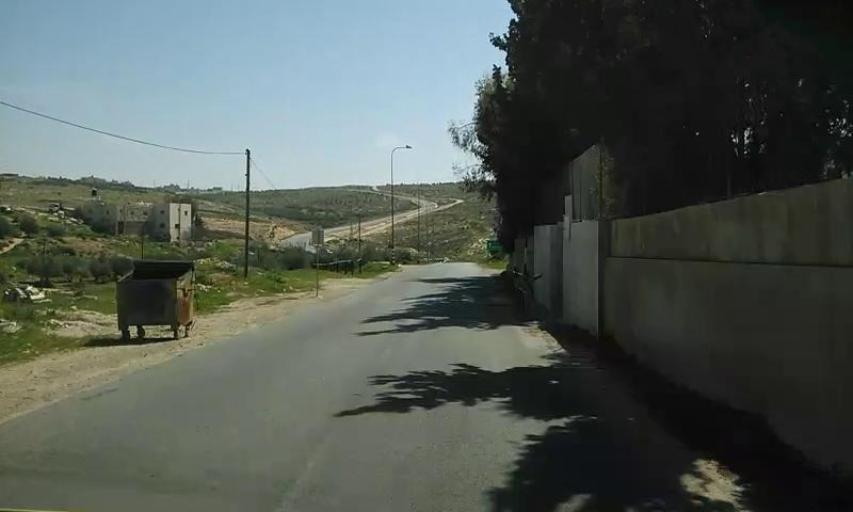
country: PS
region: West Bank
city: Marah Rabbah
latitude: 31.6279
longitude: 35.2071
